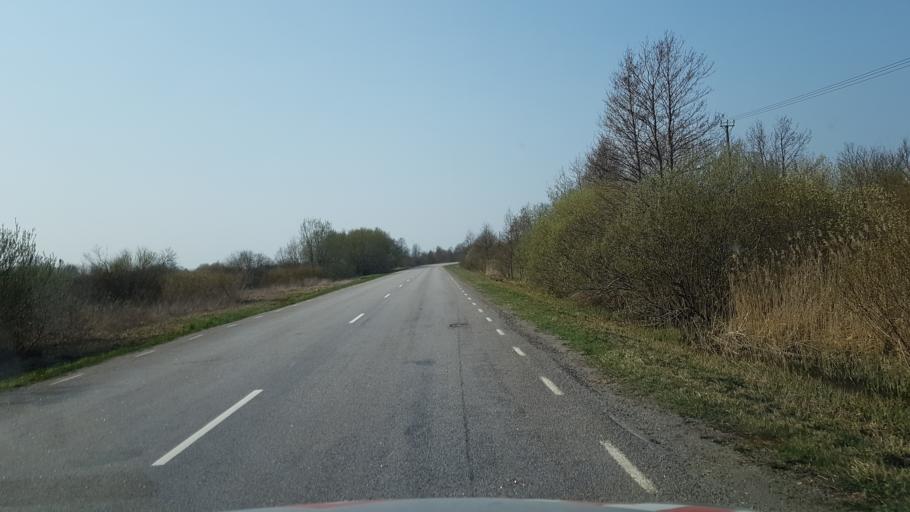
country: EE
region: Harju
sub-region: Paldiski linn
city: Paldiski
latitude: 59.3227
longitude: 24.1254
